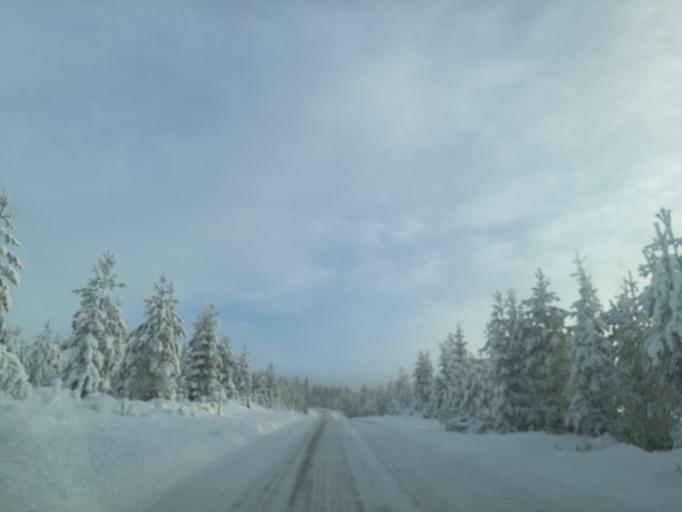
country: SE
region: Vaermland
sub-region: Torsby Kommun
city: Torsby
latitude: 60.6422
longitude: 12.7922
